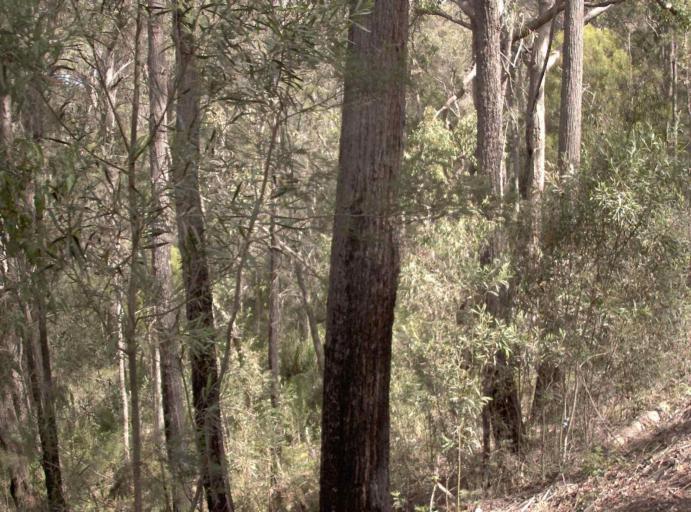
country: AU
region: New South Wales
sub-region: Bega Valley
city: Eden
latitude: -37.4972
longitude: 149.6744
